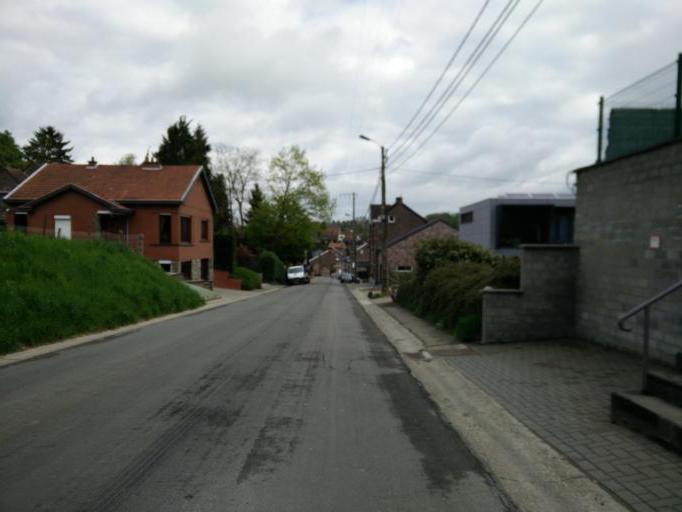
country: NL
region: Limburg
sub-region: Eijsden-Margraten
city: Eijsden
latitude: 50.7569
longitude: 5.7603
